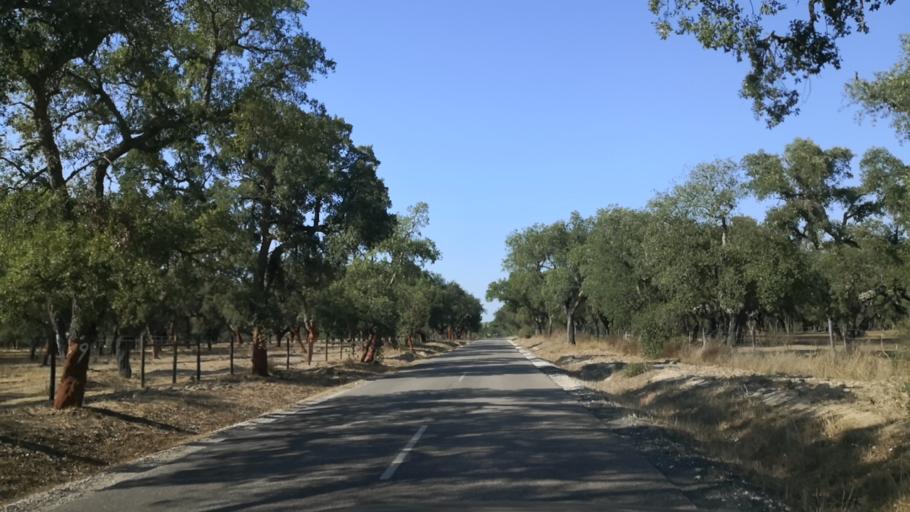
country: PT
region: Santarem
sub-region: Coruche
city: Coruche
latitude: 38.9218
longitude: -8.5236
